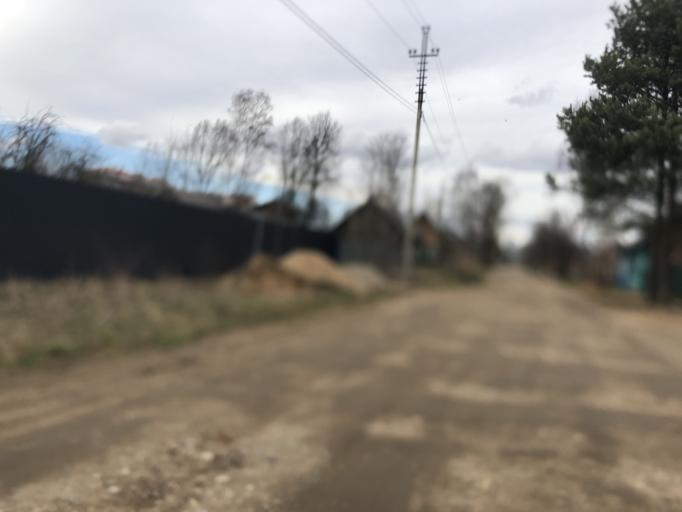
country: RU
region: Tverskaya
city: Rzhev
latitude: 56.2507
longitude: 34.3171
